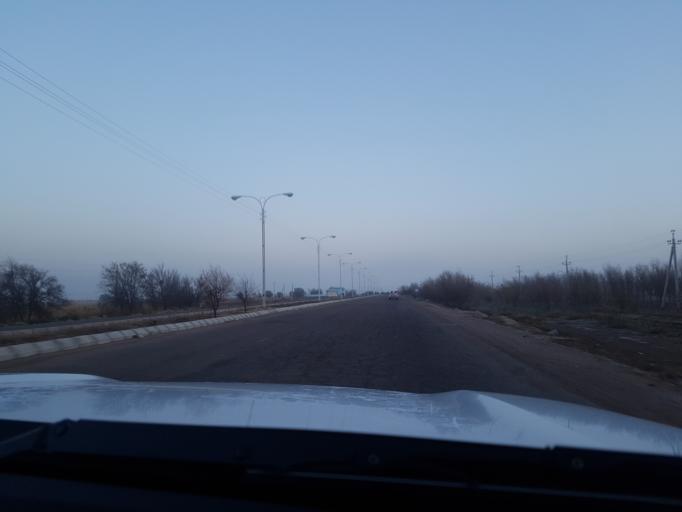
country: TM
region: Dasoguz
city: Koeneuergench
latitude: 41.7392
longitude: 58.6873
